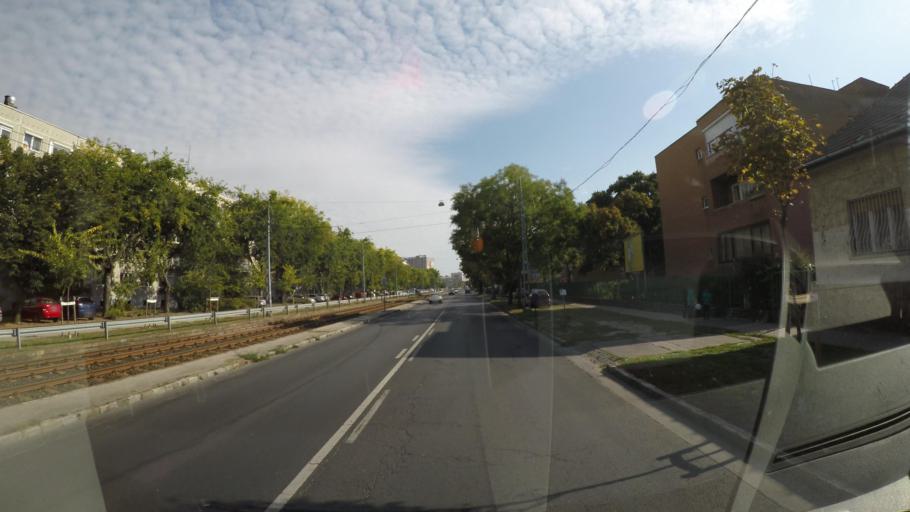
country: HU
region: Budapest
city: Budapest XIV. keruelet
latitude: 47.5083
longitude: 19.1308
